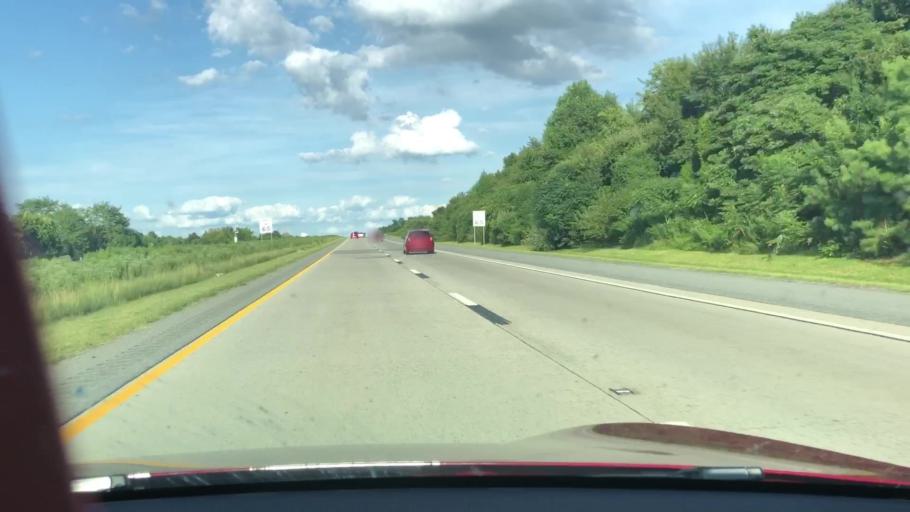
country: US
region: Delaware
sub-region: New Castle County
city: Middletown
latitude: 39.4613
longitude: -75.6638
